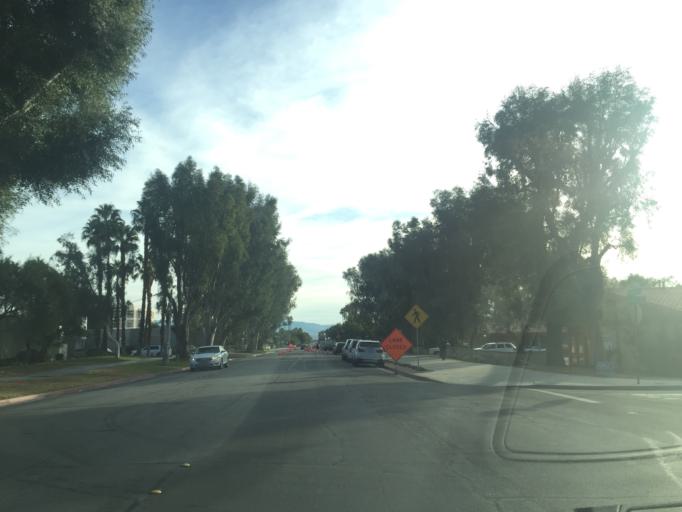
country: US
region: California
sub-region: Riverside County
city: Palm Springs
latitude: 33.8376
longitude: -116.5447
